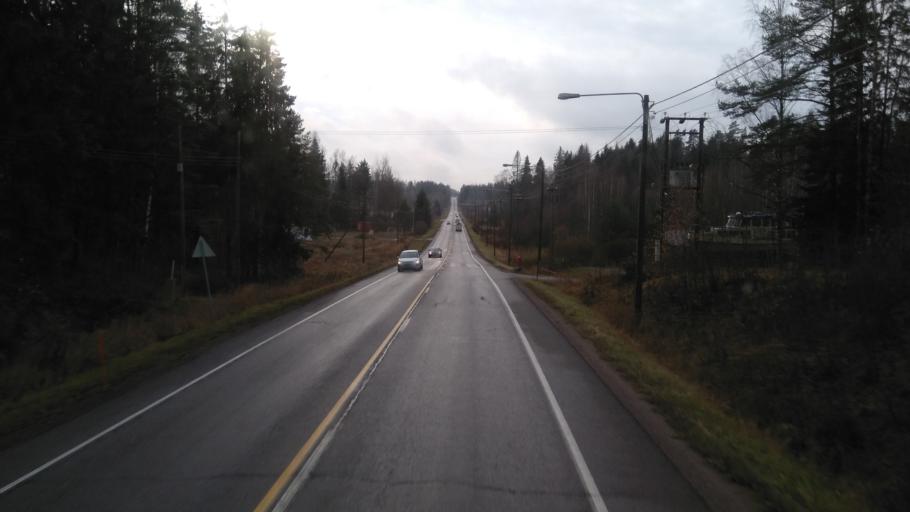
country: FI
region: Uusimaa
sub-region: Porvoo
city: Porvoo
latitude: 60.4128
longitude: 25.7002
